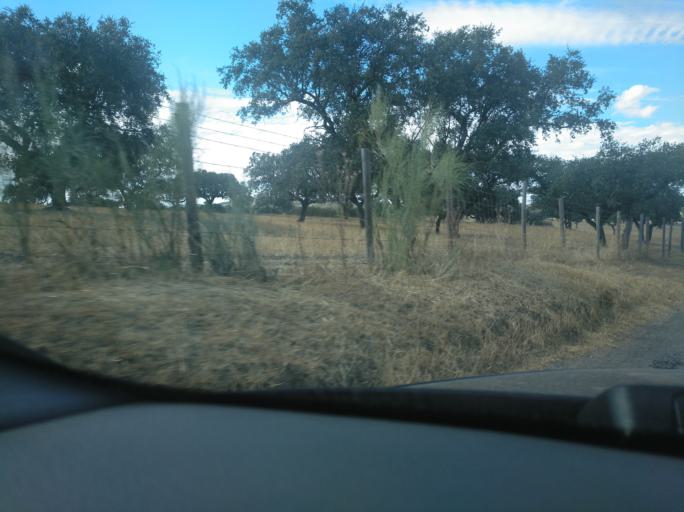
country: ES
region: Extremadura
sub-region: Provincia de Badajoz
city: La Codosera
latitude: 39.1346
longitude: -7.1562
